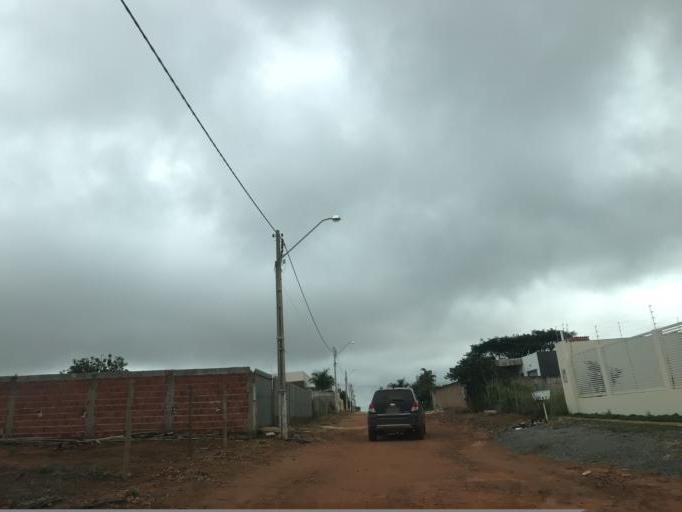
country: BR
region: Federal District
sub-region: Brasilia
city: Brasilia
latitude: -15.8302
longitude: -47.7922
